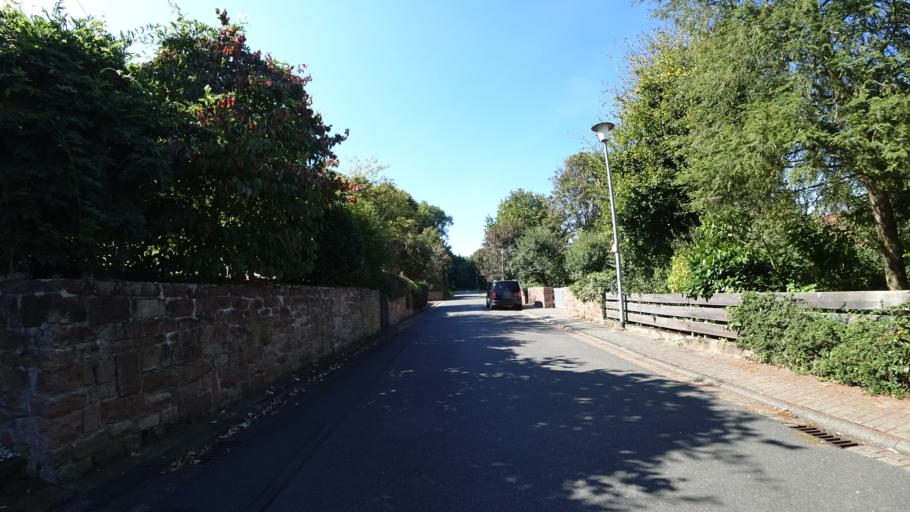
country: DE
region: Bavaria
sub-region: Regierungsbezirk Unterfranken
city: Miltenberg
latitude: 49.6980
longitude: 9.2614
